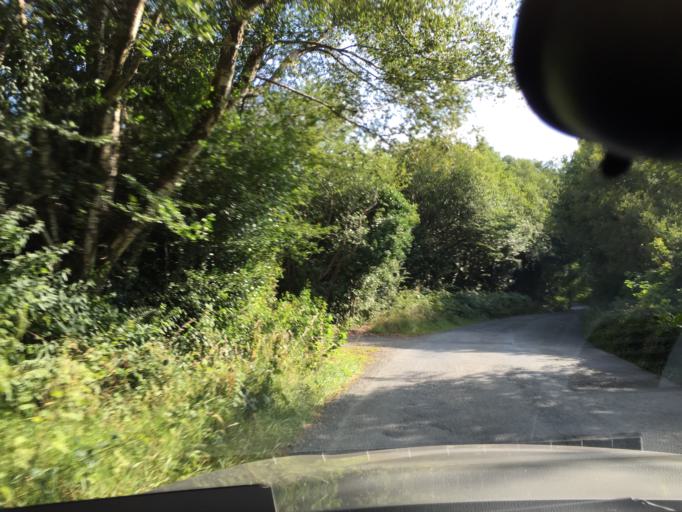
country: IE
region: Leinster
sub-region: Wicklow
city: Rathdrum
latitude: 53.0279
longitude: -6.3076
